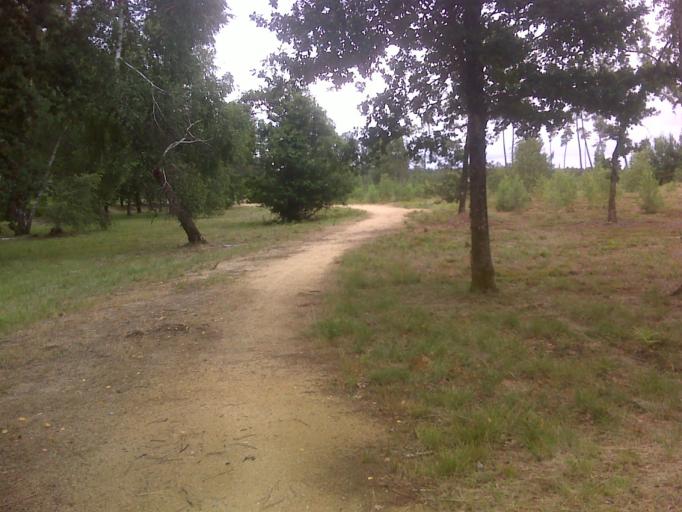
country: FR
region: Poitou-Charentes
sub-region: Departement de la Charente-Maritime
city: Montendre
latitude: 45.2725
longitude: -0.3932
